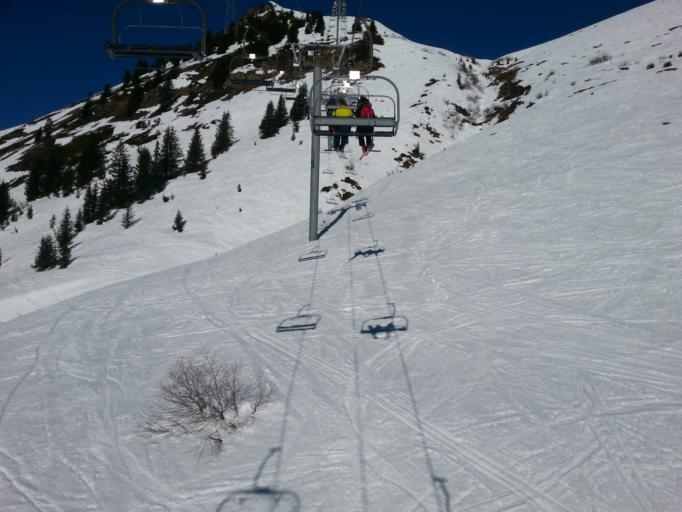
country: FR
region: Rhone-Alpes
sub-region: Departement de la Haute-Savoie
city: Samoens
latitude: 46.0255
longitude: 6.6976
